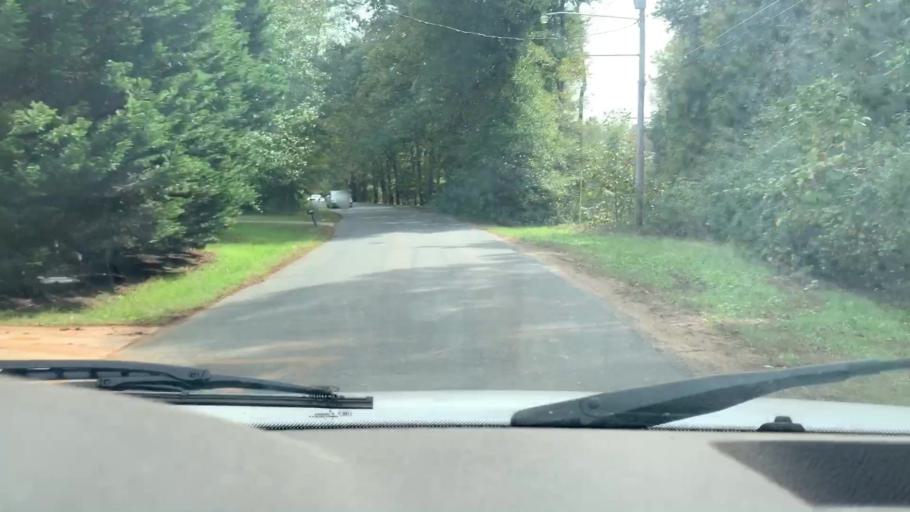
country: US
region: North Carolina
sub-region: Mecklenburg County
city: Huntersville
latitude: 35.4176
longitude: -80.8373
